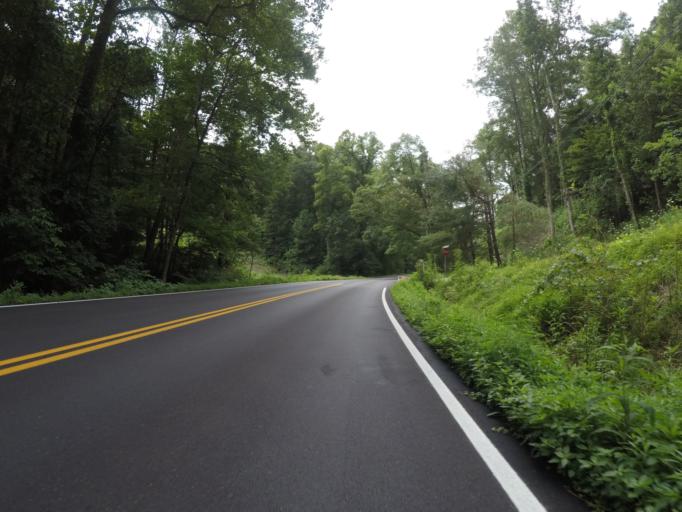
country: US
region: Kentucky
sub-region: Boyd County
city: Catlettsburg
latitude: 38.4354
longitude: -82.6274
